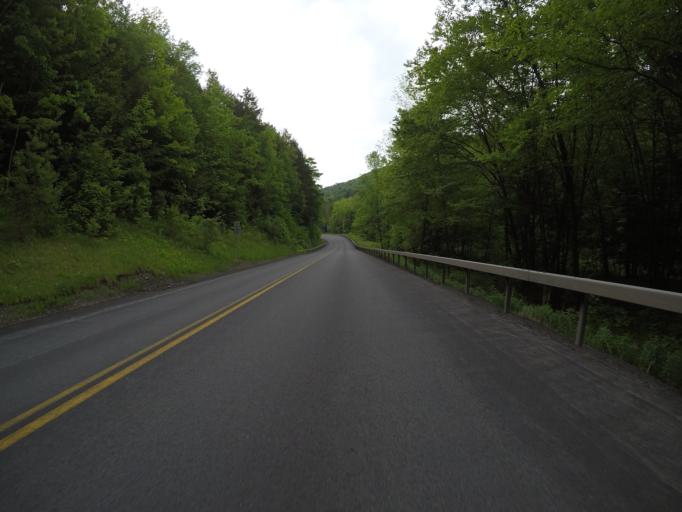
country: US
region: New York
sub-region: Sullivan County
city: Livingston Manor
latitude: 42.0680
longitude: -74.9447
